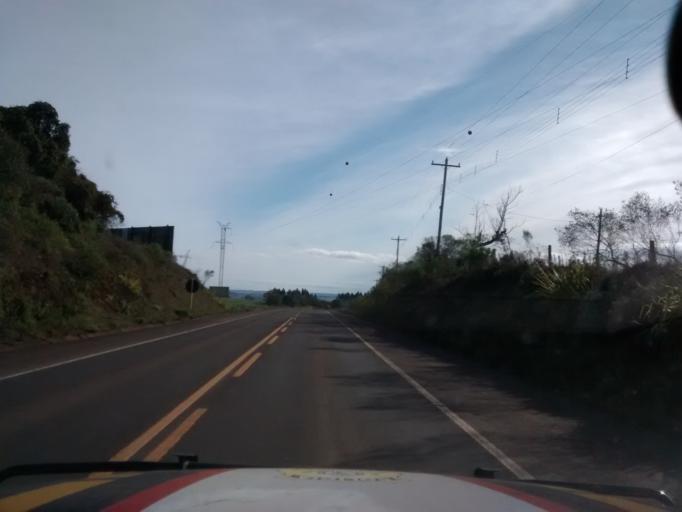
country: BR
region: Rio Grande do Sul
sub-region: Lagoa Vermelha
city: Lagoa Vermelha
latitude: -28.1828
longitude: -51.5238
